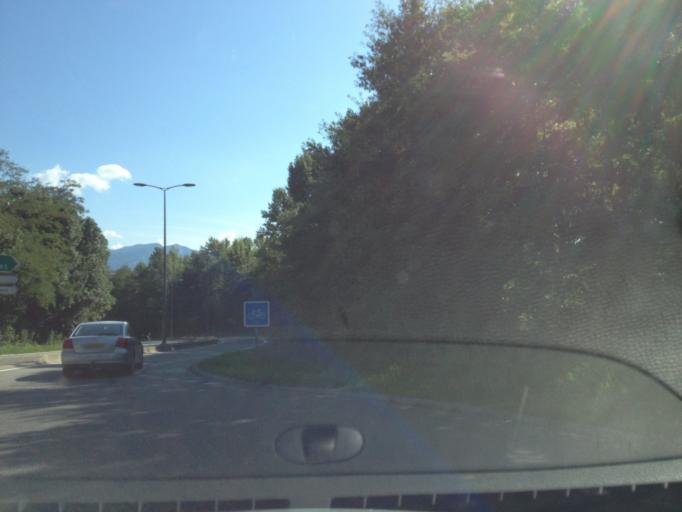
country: FR
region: Rhone-Alpes
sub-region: Departement de la Savoie
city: La Motte-Servolex
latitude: 45.5935
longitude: 5.9060
